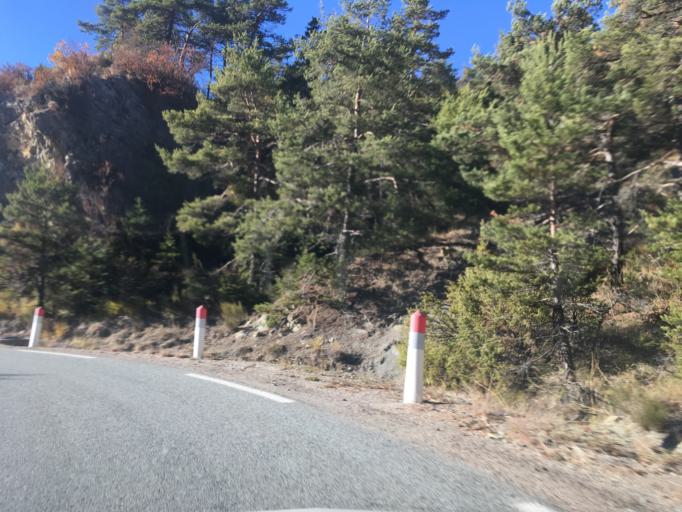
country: FR
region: Provence-Alpes-Cote d'Azur
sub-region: Departement des Alpes-de-Haute-Provence
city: Castellane
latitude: 43.7371
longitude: 6.5041
